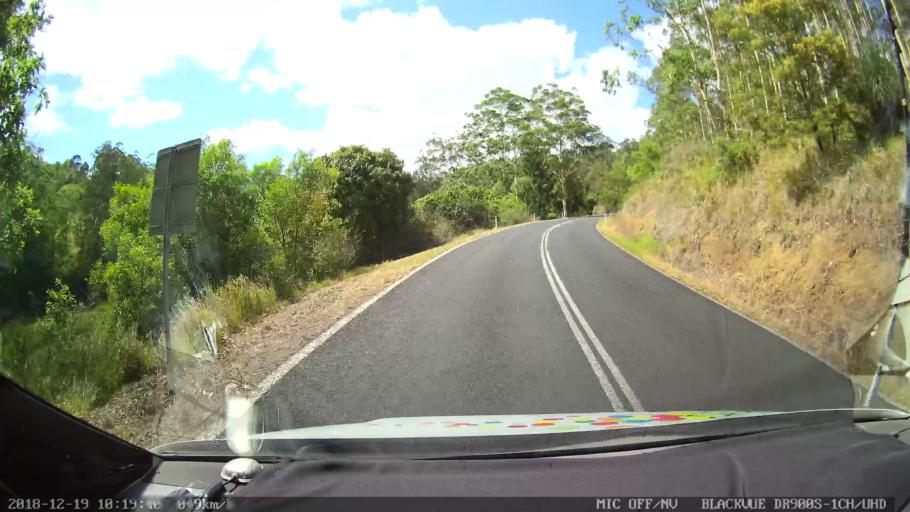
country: AU
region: New South Wales
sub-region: Kyogle
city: Kyogle
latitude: -28.5993
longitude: 153.0484
